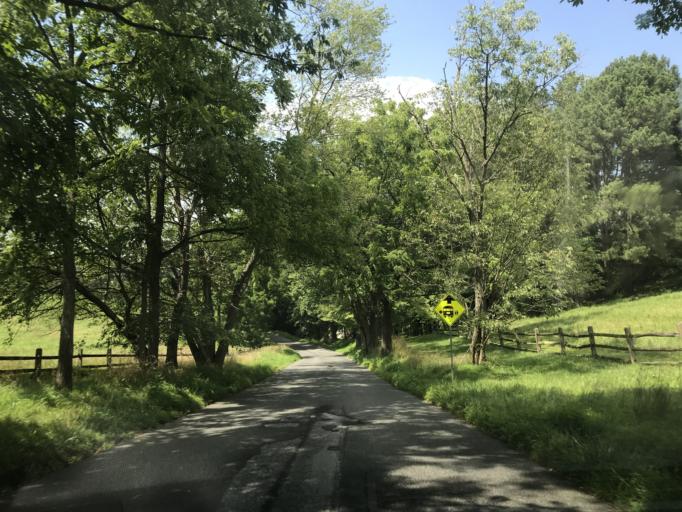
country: US
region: Delaware
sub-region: New Castle County
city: Hockessin
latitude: 39.7941
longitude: -75.6571
